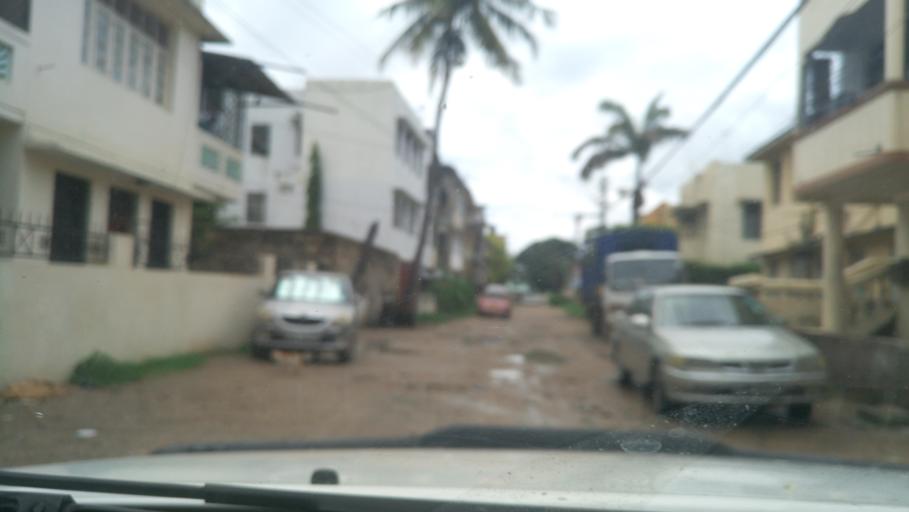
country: KE
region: Mombasa
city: Mombasa
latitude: -4.0633
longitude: 39.6655
